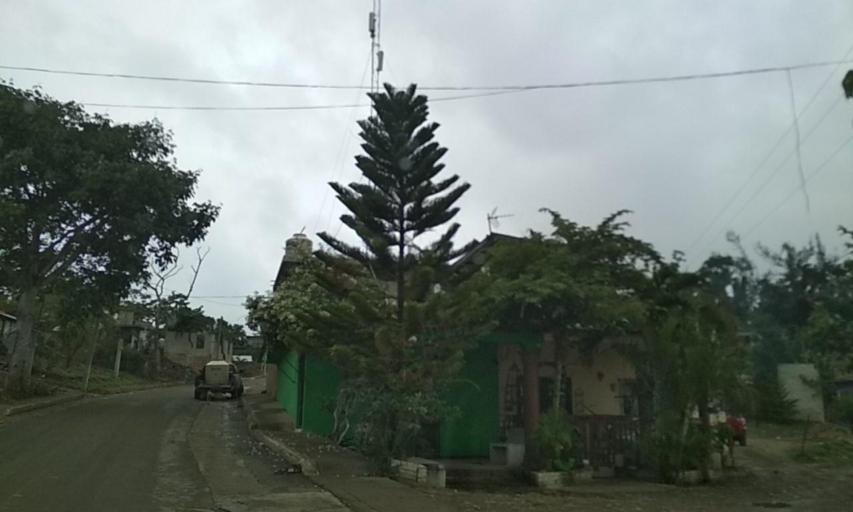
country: MX
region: Veracruz
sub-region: Papantla
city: El Chote
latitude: 20.3930
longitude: -97.3557
